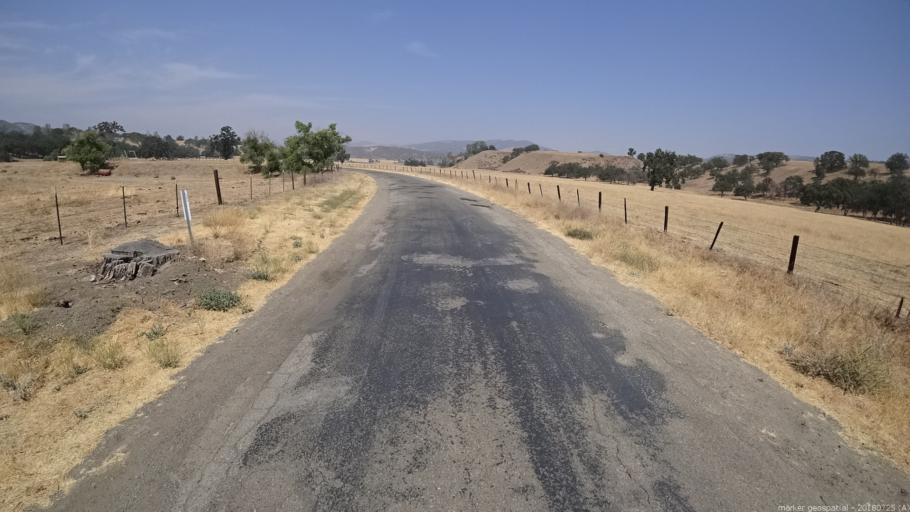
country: US
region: California
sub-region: Fresno County
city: Coalinga
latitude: 35.9082
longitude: -120.4345
